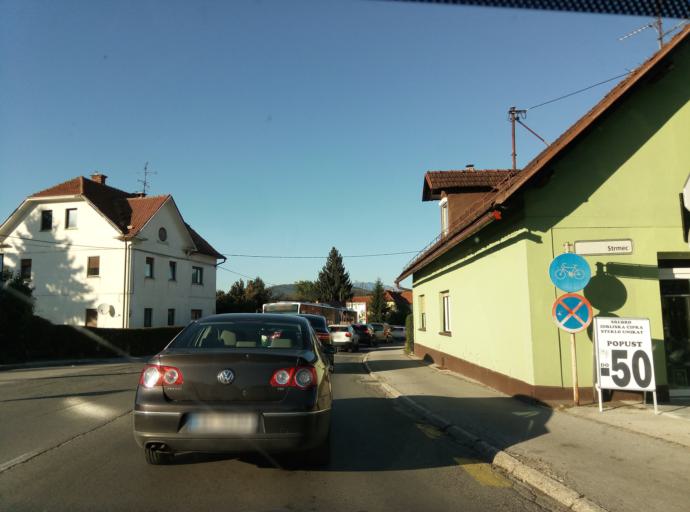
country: SI
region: Ljubljana
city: Ljubljana
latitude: 46.0910
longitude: 14.5139
